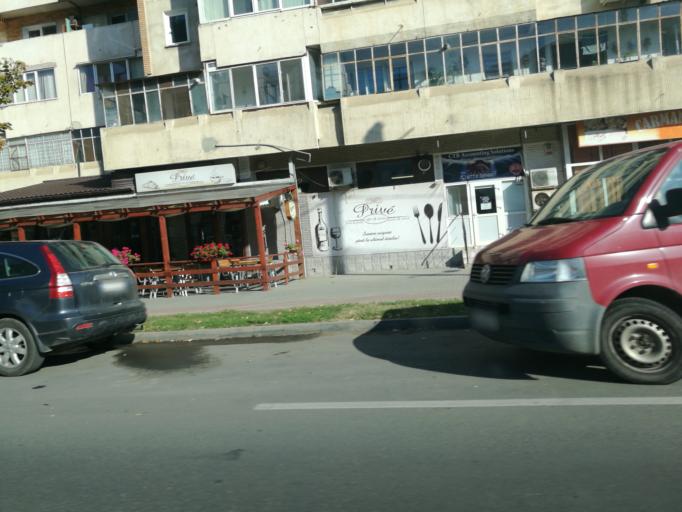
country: RO
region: Iasi
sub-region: Comuna Miroslava
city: Miroslava
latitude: 47.1747
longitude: 27.5477
